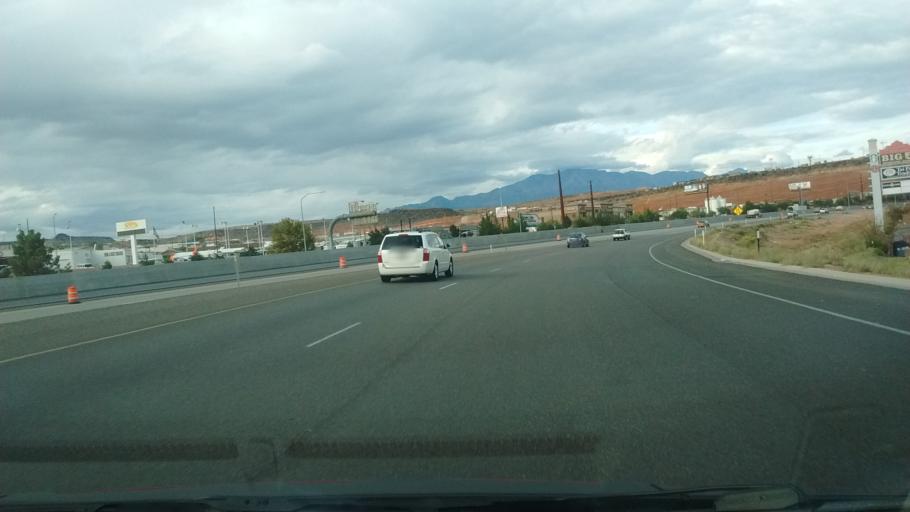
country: US
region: Utah
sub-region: Washington County
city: Saint George
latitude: 37.1117
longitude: -113.5565
